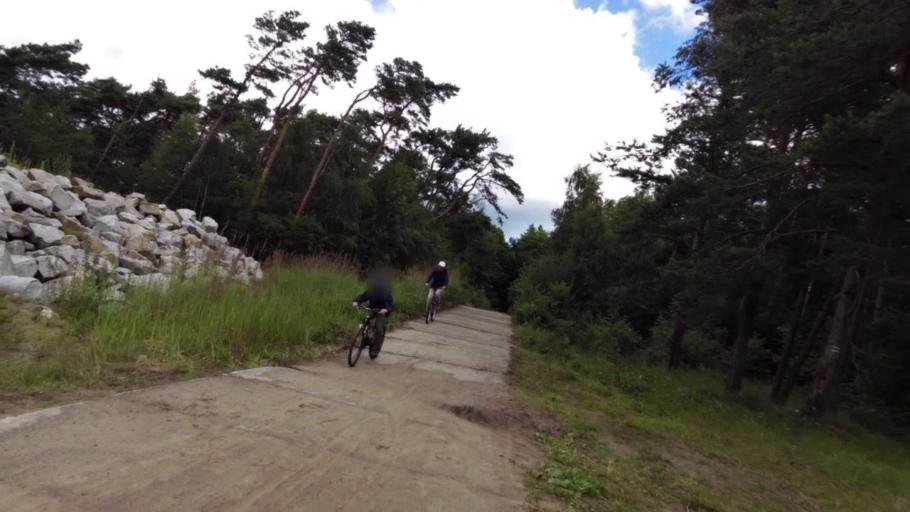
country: PL
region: West Pomeranian Voivodeship
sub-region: Powiat slawienski
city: Darlowo
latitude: 54.4906
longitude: 16.4395
